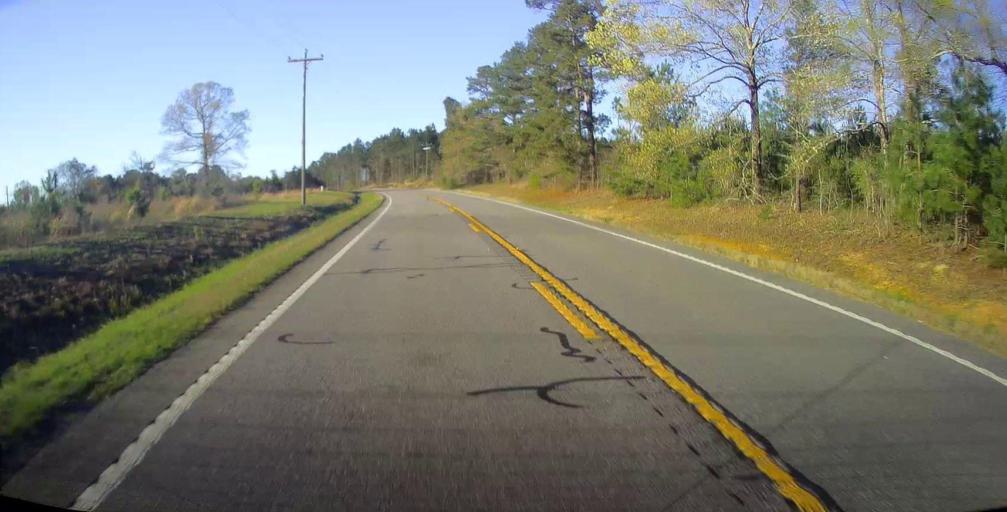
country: US
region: Georgia
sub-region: Wilcox County
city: Abbeville
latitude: 32.0237
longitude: -83.2490
